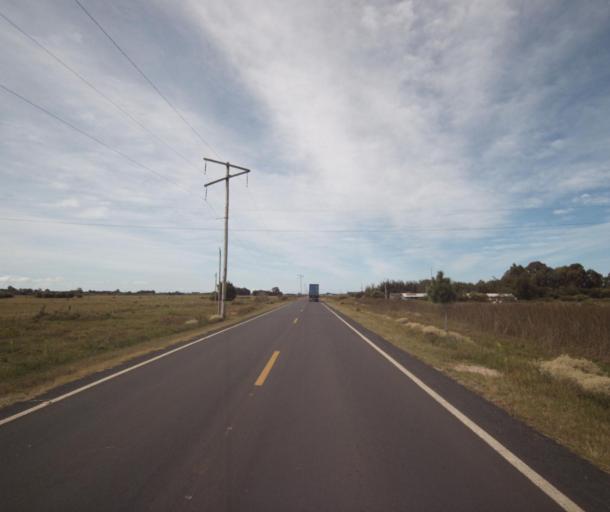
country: BR
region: Rio Grande do Sul
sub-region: Rio Grande
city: Rio Grande
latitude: -31.9419
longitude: -51.9733
